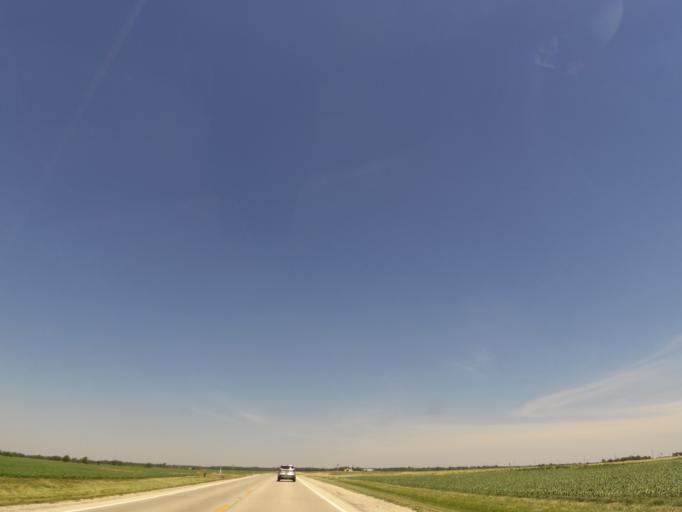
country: US
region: Illinois
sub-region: Iroquois County
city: Milford
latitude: 40.5735
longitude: -87.6941
